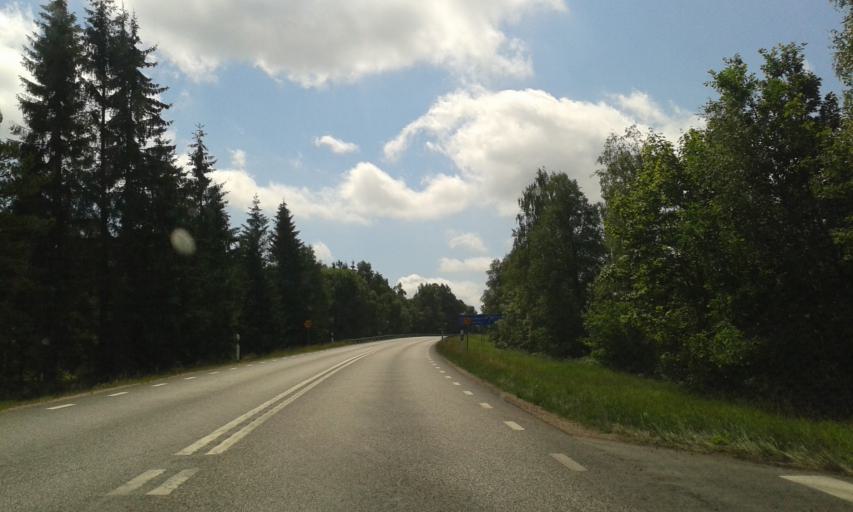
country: SE
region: Joenkoeping
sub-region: Varnamo Kommun
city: Bredaryd
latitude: 57.1748
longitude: 13.7626
